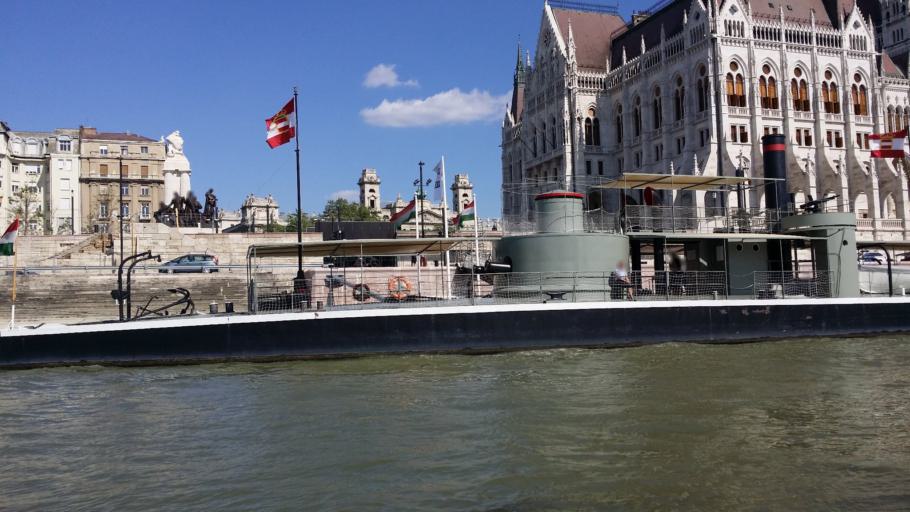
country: HU
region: Budapest
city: Budapest
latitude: 47.5088
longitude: 19.0444
